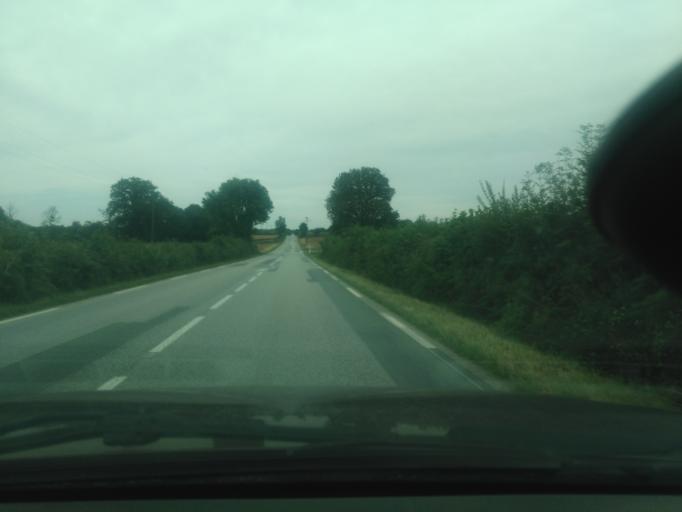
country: FR
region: Poitou-Charentes
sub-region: Departement des Deux-Sevres
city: Moncoutant
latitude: 46.6325
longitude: -0.5482
